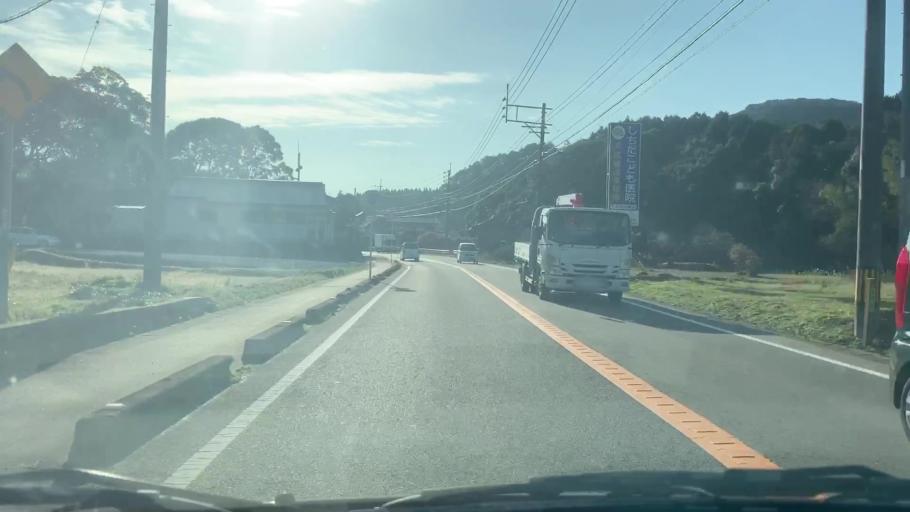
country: JP
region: Saga Prefecture
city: Takeocho-takeo
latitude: 33.2463
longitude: 130.0049
